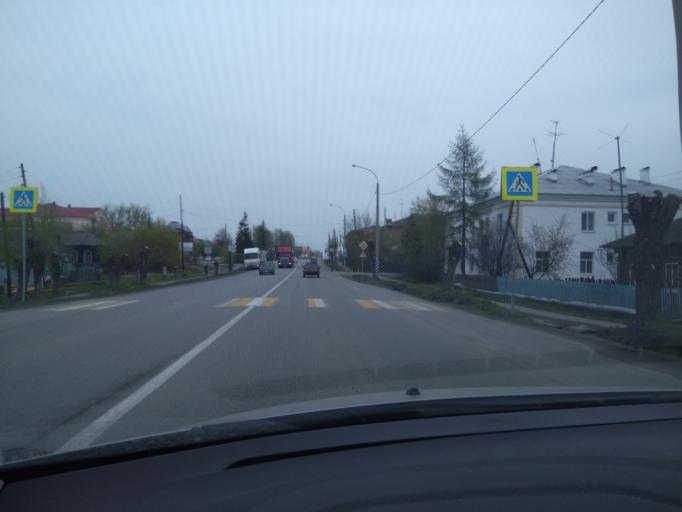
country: RU
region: Sverdlovsk
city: Beloyarskiy
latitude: 56.7596
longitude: 61.4103
